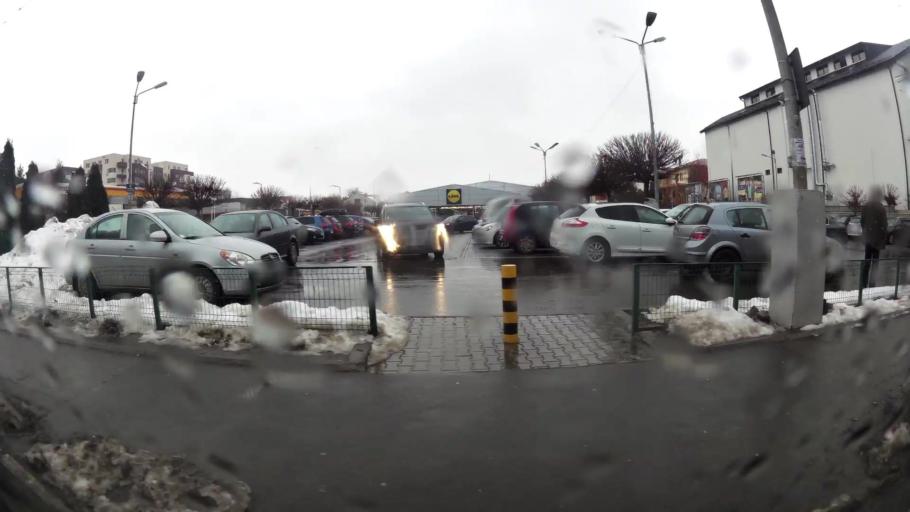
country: RO
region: Ilfov
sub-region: Comuna Chiajna
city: Rosu
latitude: 44.4173
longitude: 26.0137
